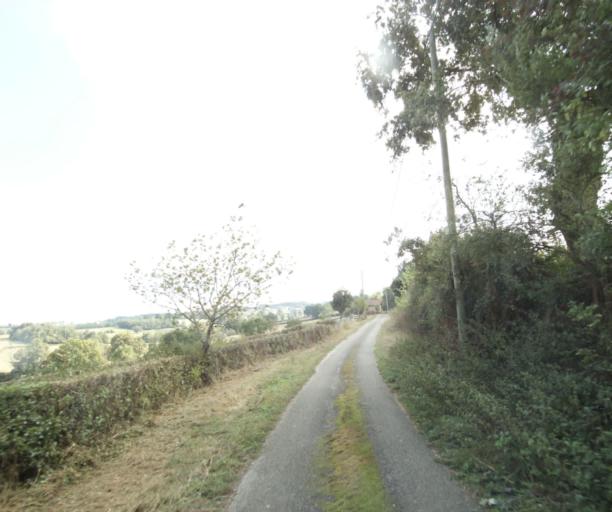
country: FR
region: Bourgogne
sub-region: Departement de Saone-et-Loire
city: Charolles
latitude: 46.3553
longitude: 4.2446
